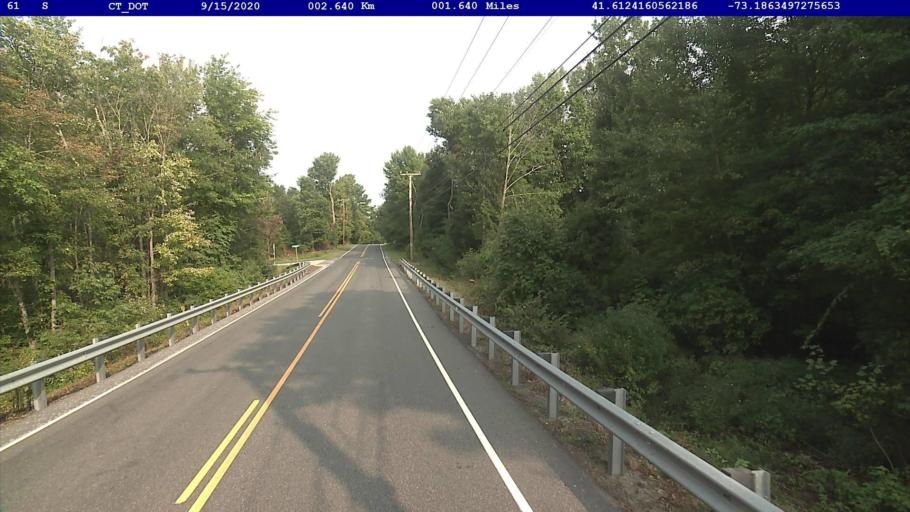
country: US
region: Connecticut
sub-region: Litchfield County
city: Bethlehem Village
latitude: 41.6124
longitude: -73.1863
